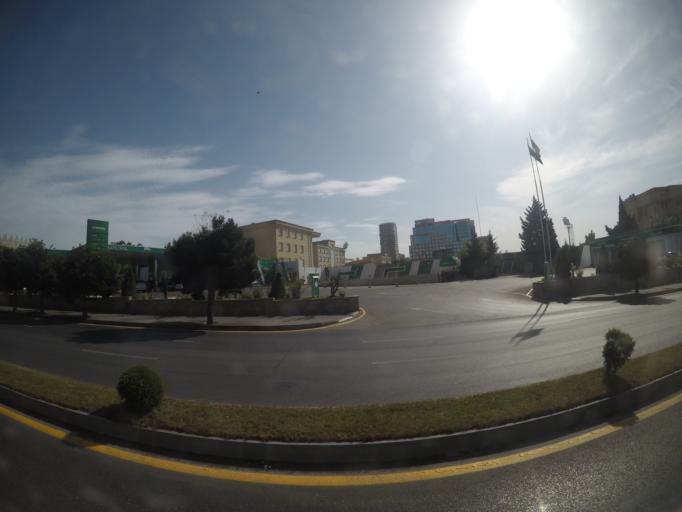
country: AZ
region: Baki
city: Badamdar
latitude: 40.3887
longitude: 49.8262
